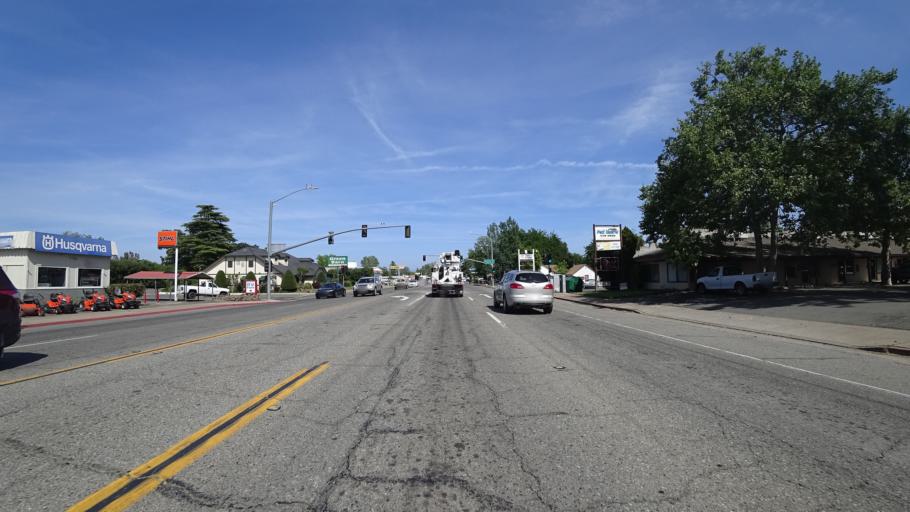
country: US
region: California
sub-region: Tehama County
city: Red Bluff
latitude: 40.1861
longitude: -122.2099
